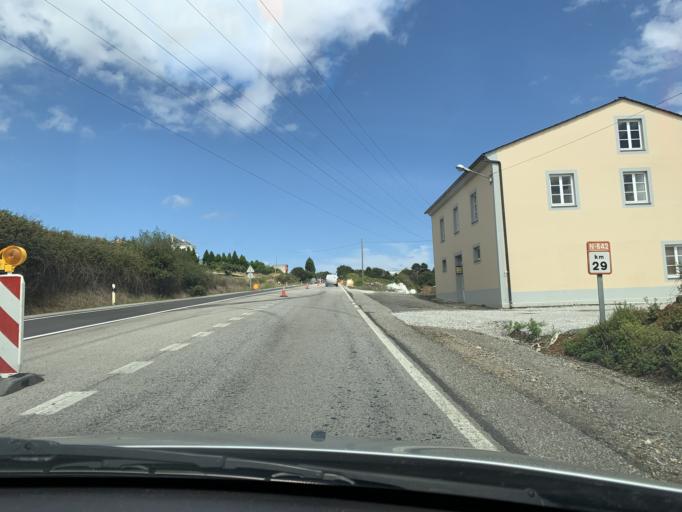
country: ES
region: Galicia
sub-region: Provincia de Lugo
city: Foz
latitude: 43.5468
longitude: -7.2705
